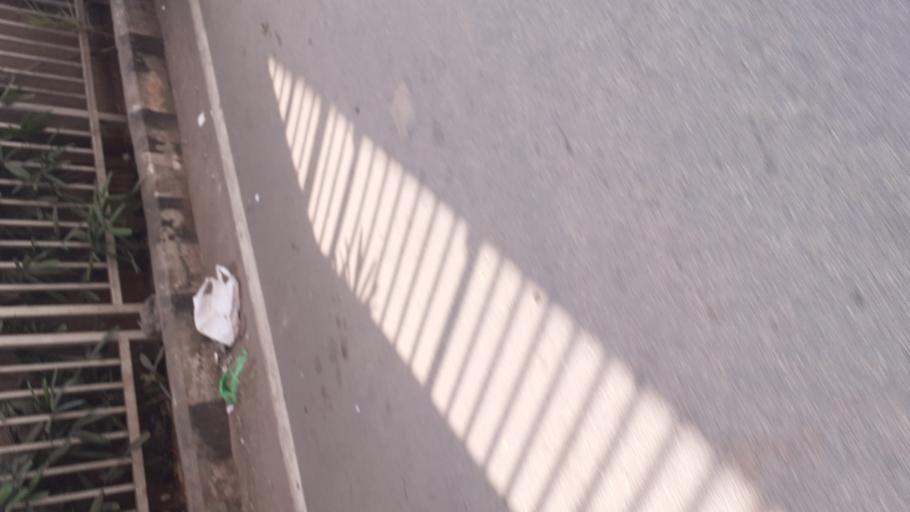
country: IN
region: Telangana
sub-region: Rangareddi
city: Kukatpalli
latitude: 17.4420
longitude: 78.4413
